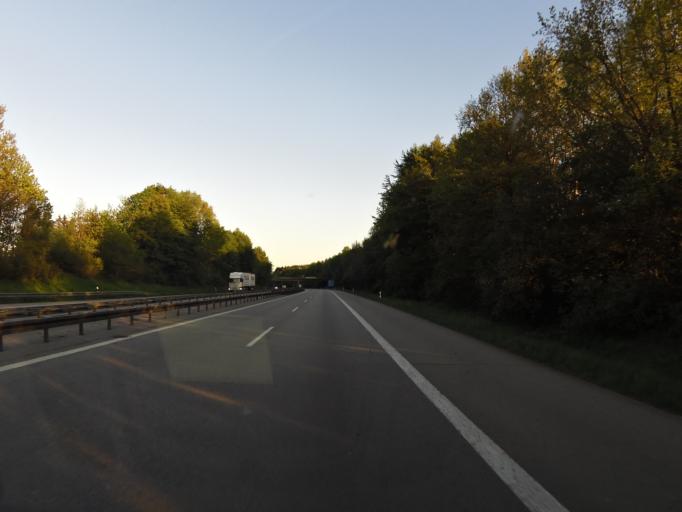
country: DE
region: Bavaria
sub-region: Lower Bavaria
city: Aussernzell
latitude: 48.6977
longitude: 13.1922
